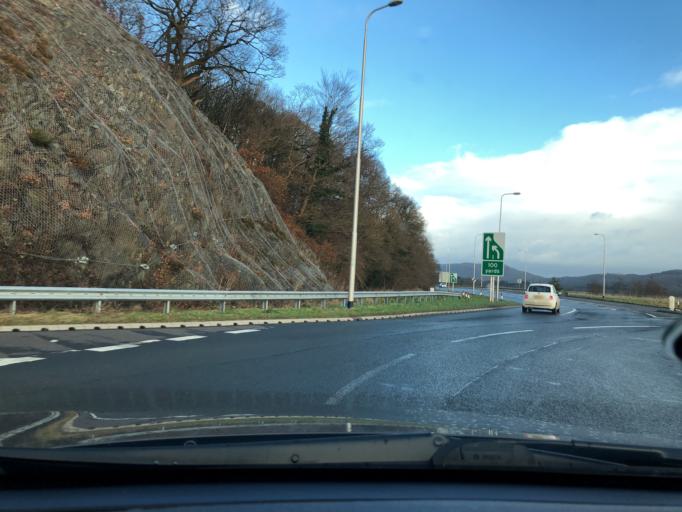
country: GB
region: England
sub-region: Cumbria
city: Ulverston
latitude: 54.2353
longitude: -3.0505
